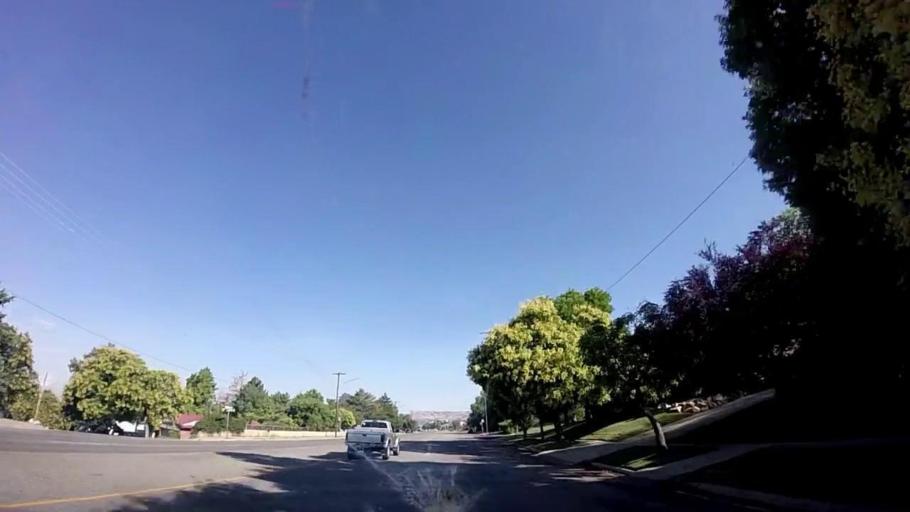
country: US
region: Utah
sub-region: Salt Lake County
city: Canyon Rim
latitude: 40.7302
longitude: -111.8177
